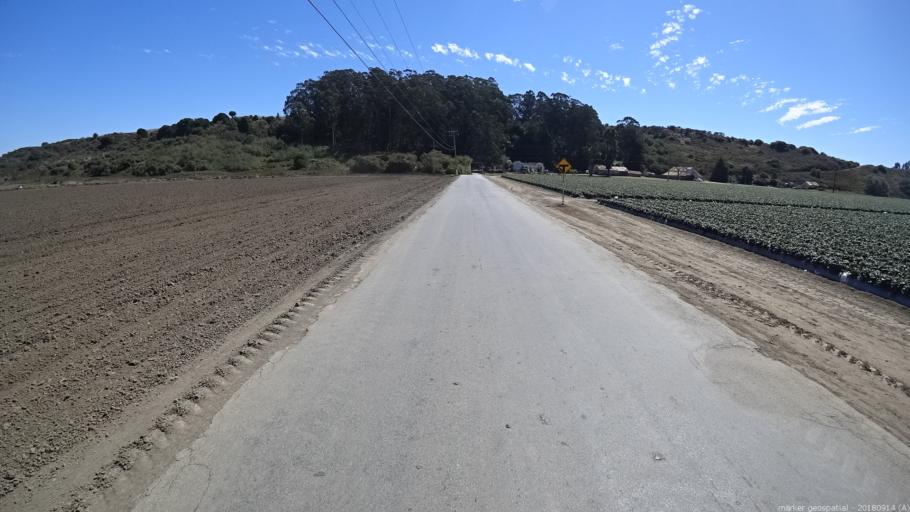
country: US
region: California
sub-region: Santa Cruz County
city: Watsonville
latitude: 36.8721
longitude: -121.7863
